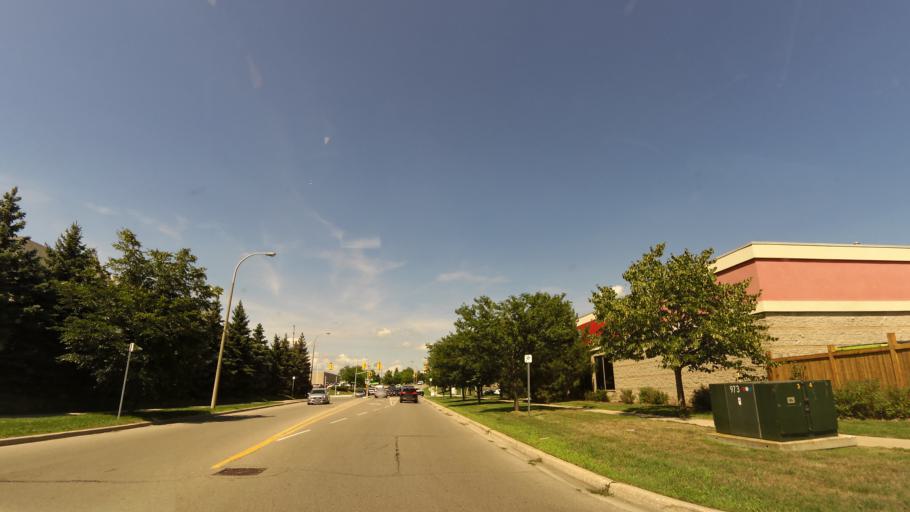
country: CA
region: Ontario
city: Ancaster
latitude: 43.2265
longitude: -79.9419
